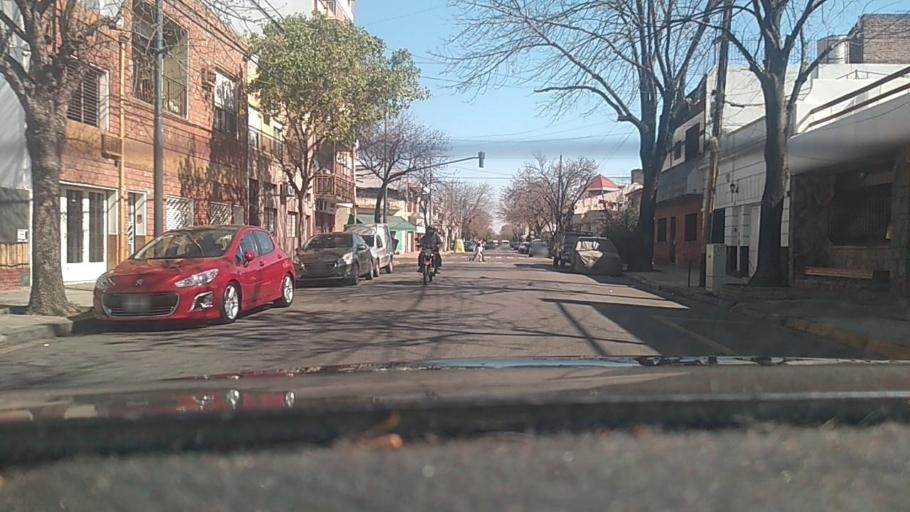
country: AR
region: Buenos Aires F.D.
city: Villa Santa Rita
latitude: -34.6106
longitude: -58.5002
